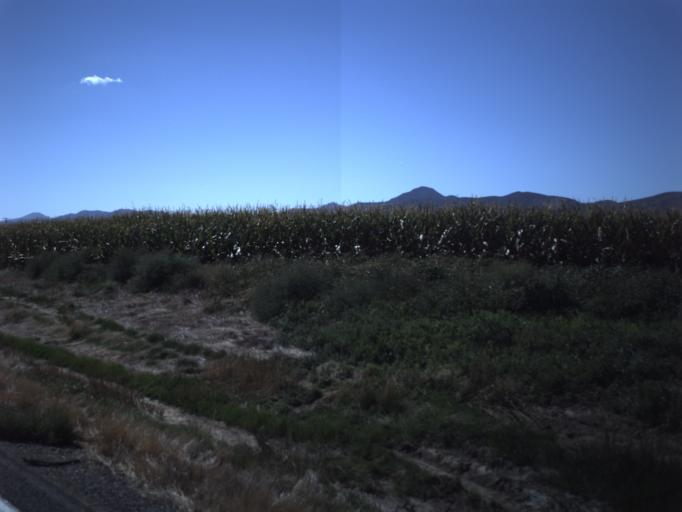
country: US
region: Utah
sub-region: Utah County
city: Genola
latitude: 40.0872
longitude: -111.9589
